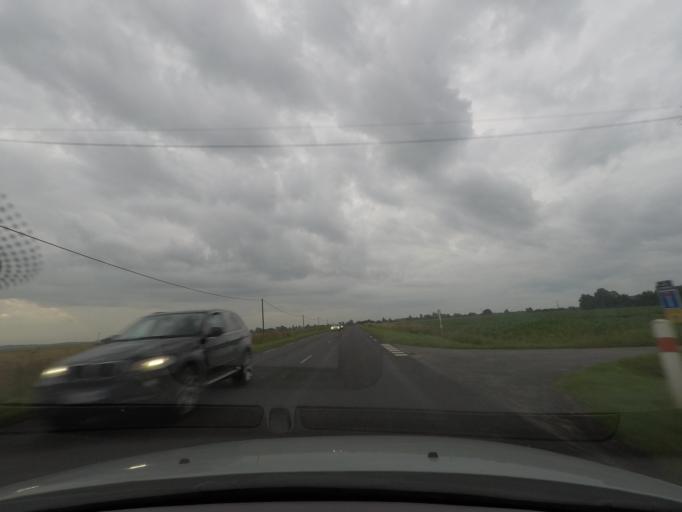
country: FR
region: Haute-Normandie
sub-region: Departement de la Seine-Maritime
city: Neufchatel-en-Bray
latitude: 49.7360
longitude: 1.4973
